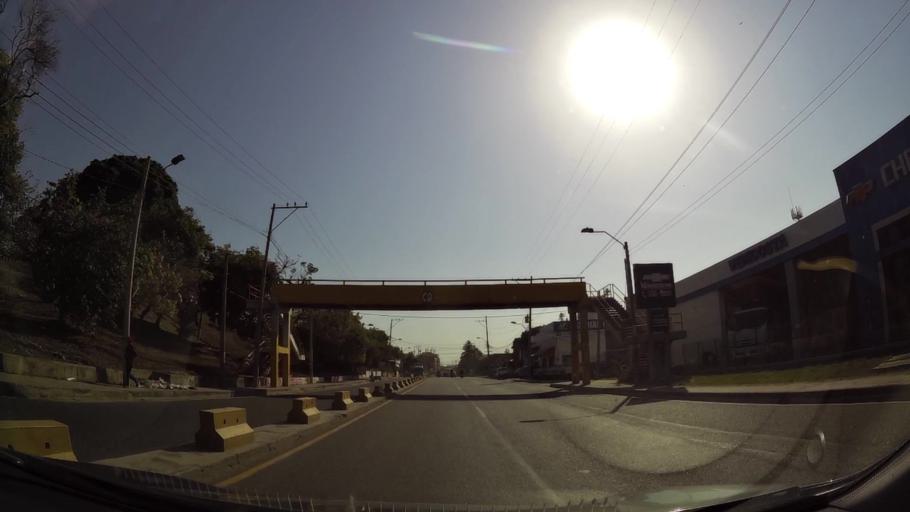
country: CO
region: Bolivar
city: Cartagena
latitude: 10.3886
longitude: -75.5176
